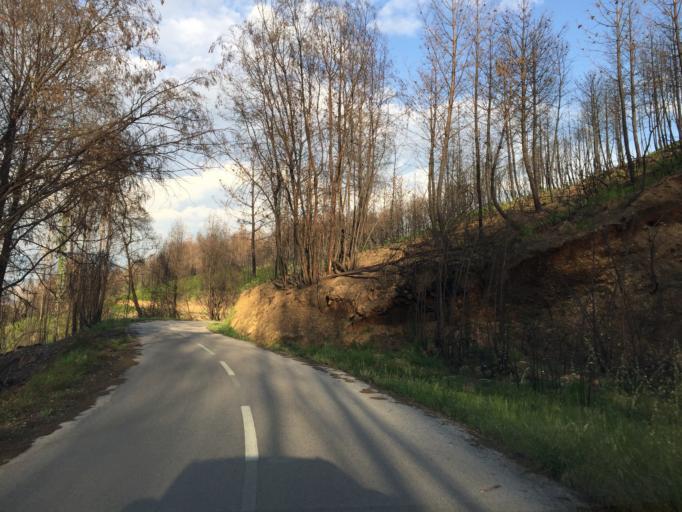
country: PT
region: Coimbra
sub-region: Pampilhosa da Serra
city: Pampilhosa da Serra
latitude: 40.1347
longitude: -7.9962
